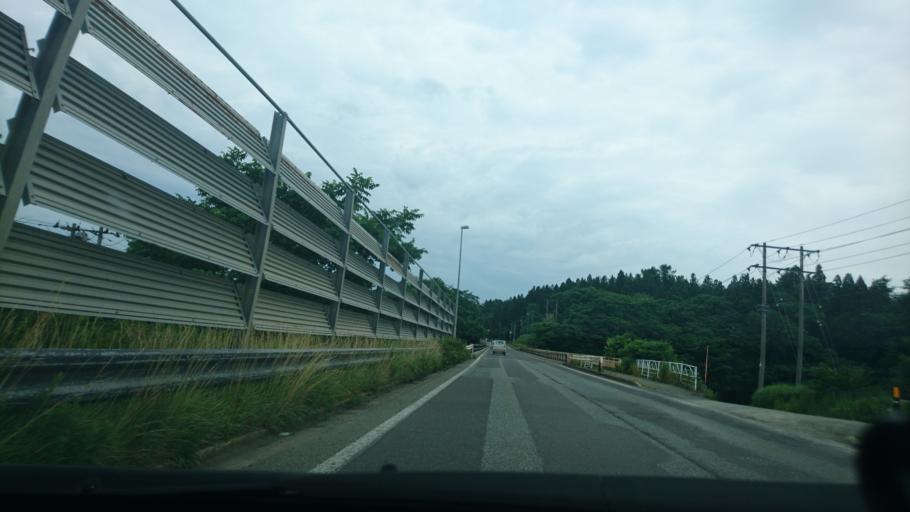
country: JP
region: Akita
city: Yokotemachi
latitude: 39.3334
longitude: 140.5593
